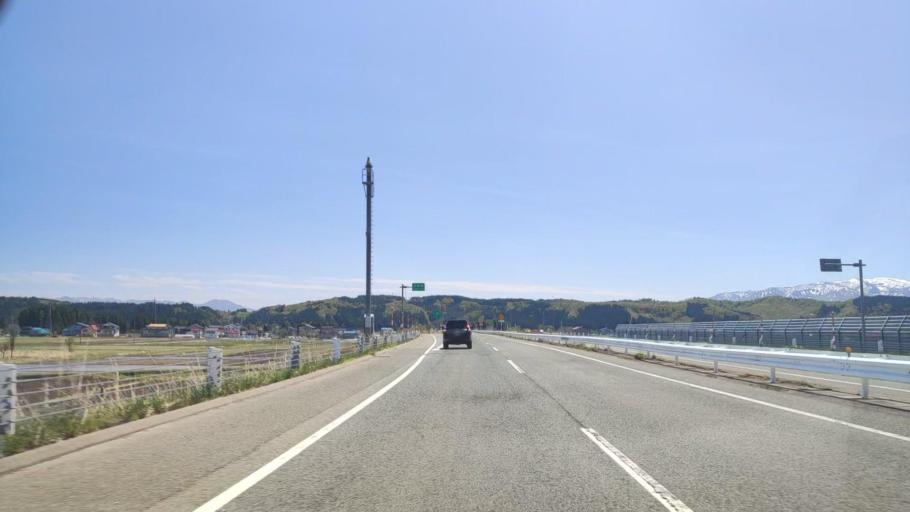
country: JP
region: Yamagata
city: Shinjo
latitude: 38.7069
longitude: 140.3089
